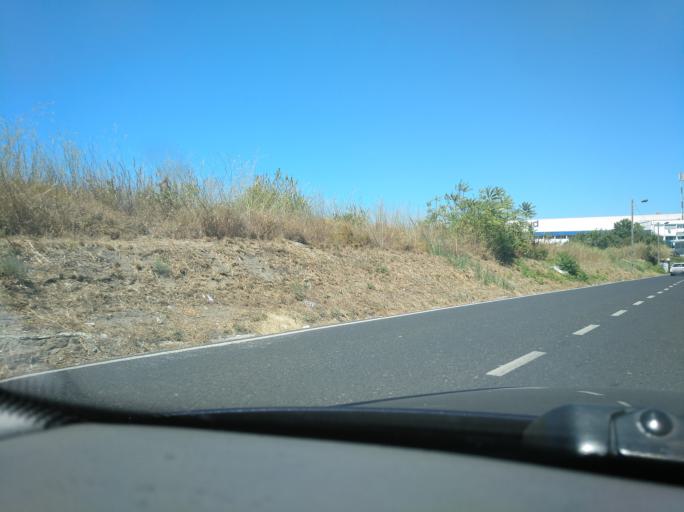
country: PT
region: Lisbon
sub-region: Loures
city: Apelacao
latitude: 38.8050
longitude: -9.1451
